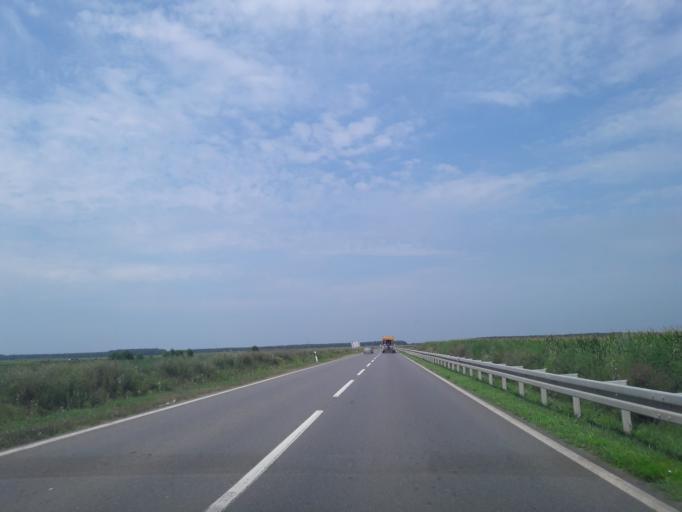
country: HR
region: Osjecko-Baranjska
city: Cepin
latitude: 45.5158
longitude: 18.5321
